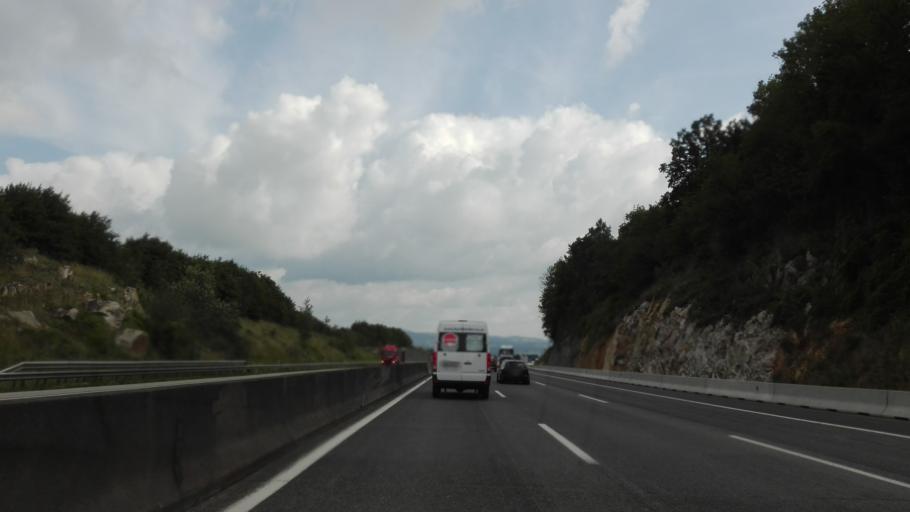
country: AT
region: Lower Austria
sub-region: Politischer Bezirk Melk
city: Erlauf
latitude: 48.1797
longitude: 15.1874
